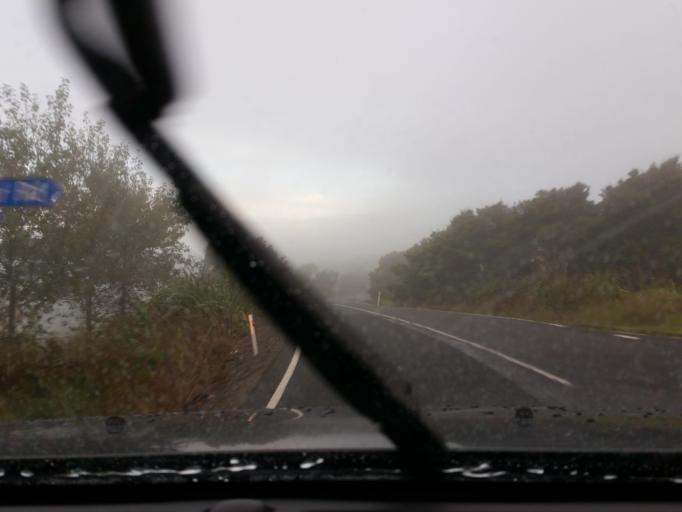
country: NZ
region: Northland
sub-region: Kaipara District
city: Dargaville
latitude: -35.9517
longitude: 173.9206
